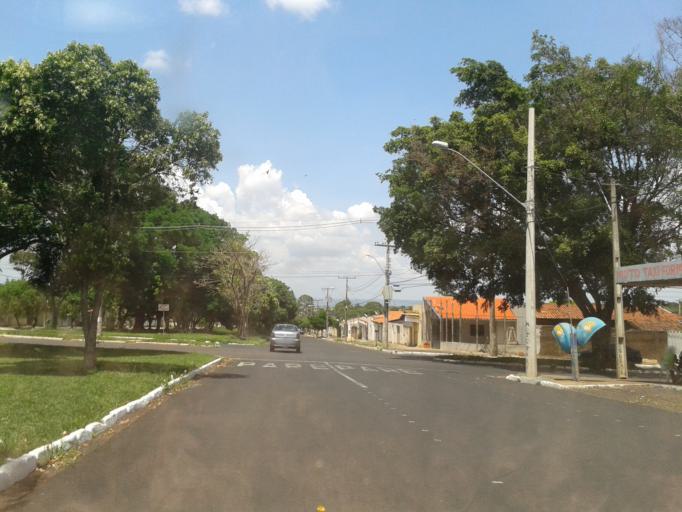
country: BR
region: Minas Gerais
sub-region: Araguari
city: Araguari
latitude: -18.6674
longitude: -48.1988
